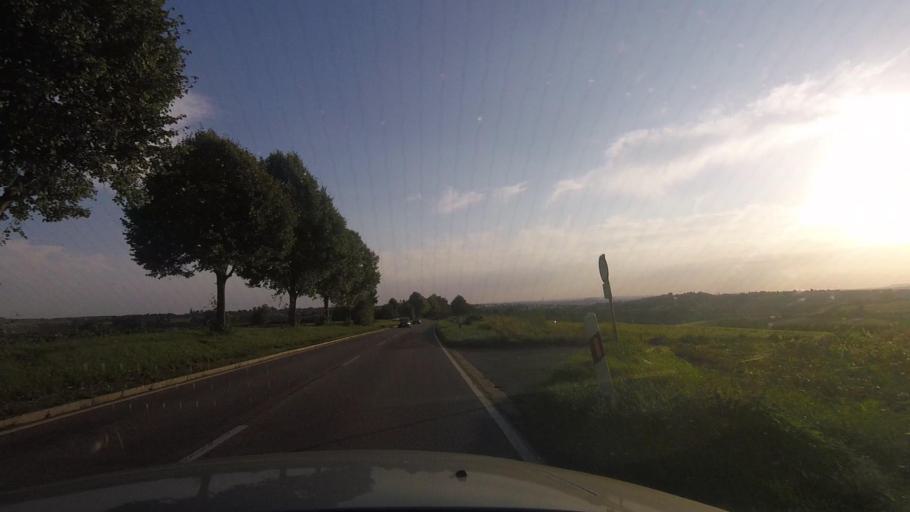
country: DE
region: Baden-Wuerttemberg
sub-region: Regierungsbezirk Stuttgart
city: Kirchberg an der Murr
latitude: 48.9565
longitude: 9.3167
